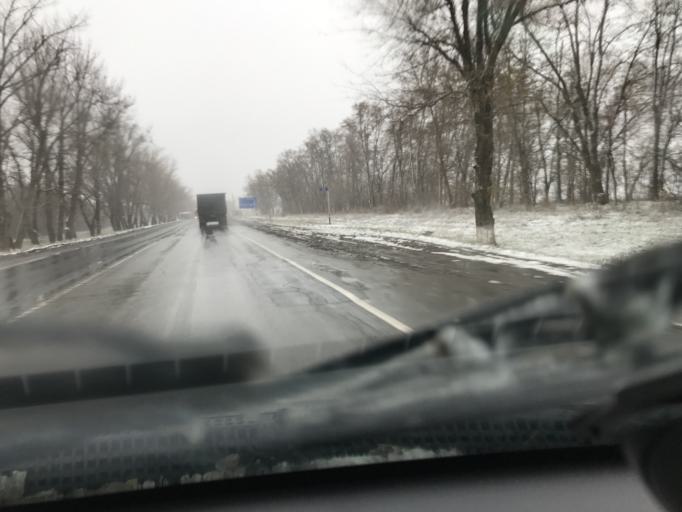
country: RU
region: Rostov
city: Yegorlykskaya
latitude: 46.5906
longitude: 40.6287
